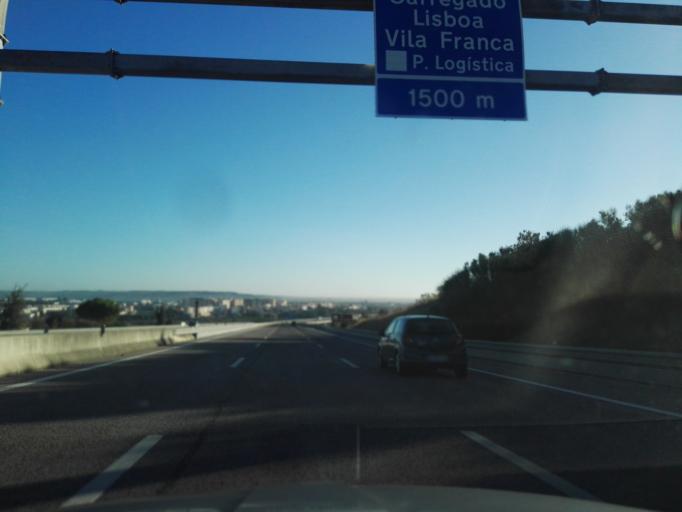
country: PT
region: Lisbon
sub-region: Alenquer
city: Carregado
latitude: 39.0137
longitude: -8.9907
